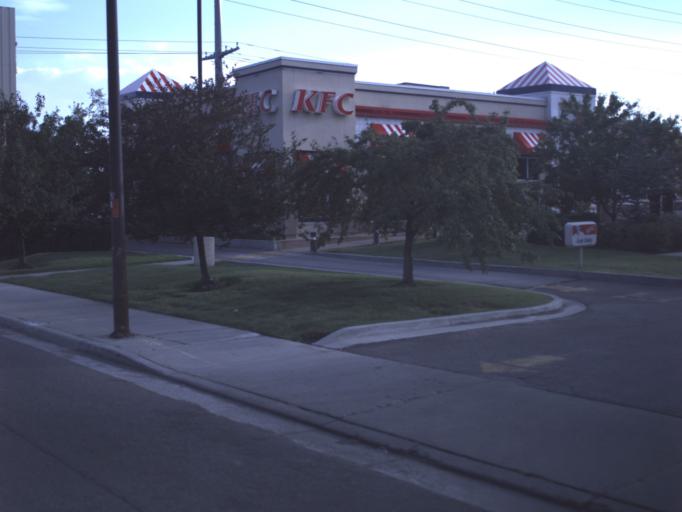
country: US
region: Utah
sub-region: Salt Lake County
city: Centerfield
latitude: 40.6876
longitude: -111.8884
